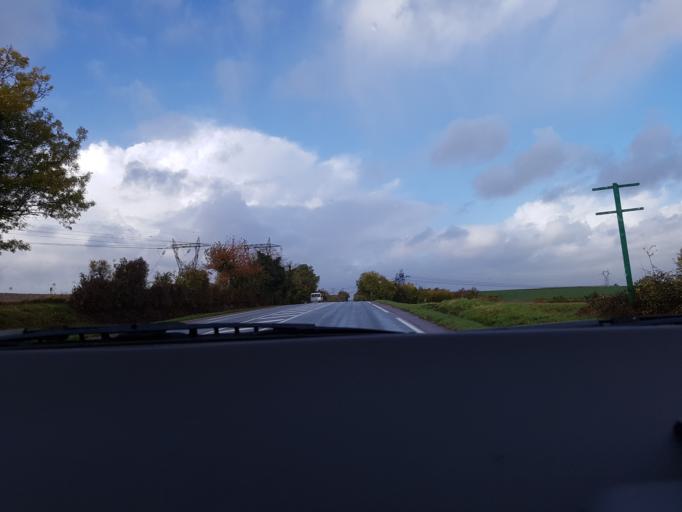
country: FR
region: Poitou-Charentes
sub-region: Departement de la Charente-Maritime
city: Les Gonds
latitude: 45.6713
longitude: -0.6010
